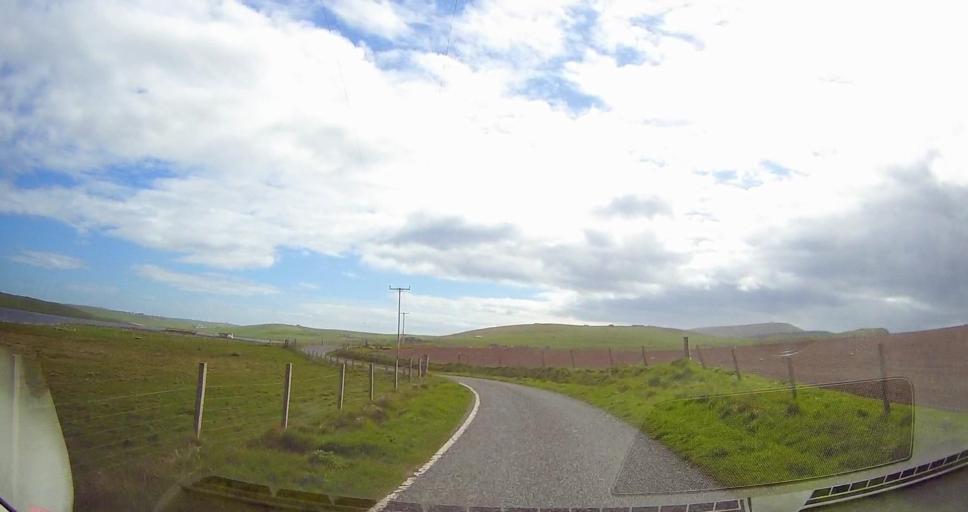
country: GB
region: Scotland
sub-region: Shetland Islands
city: Sandwick
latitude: 59.9403
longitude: -1.3463
